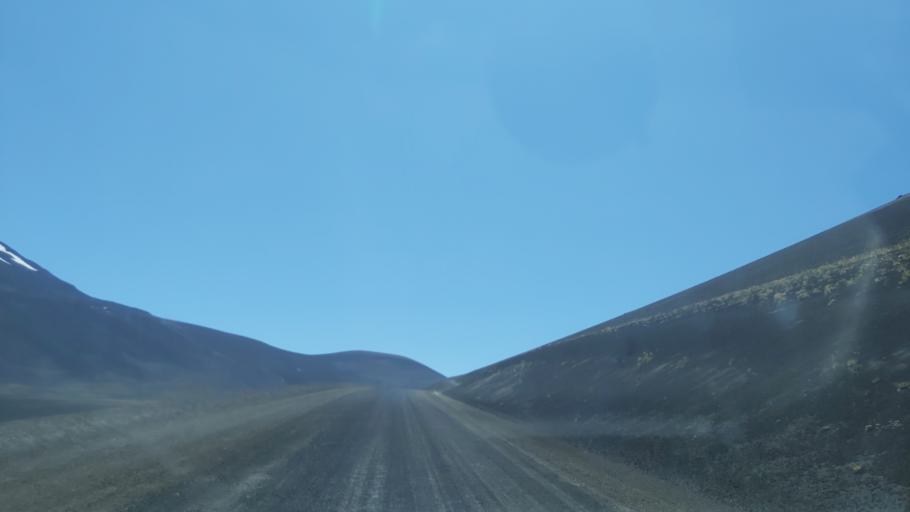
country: CL
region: Araucania
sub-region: Provincia de Cautin
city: Vilcun
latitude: -38.4041
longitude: -71.5441
